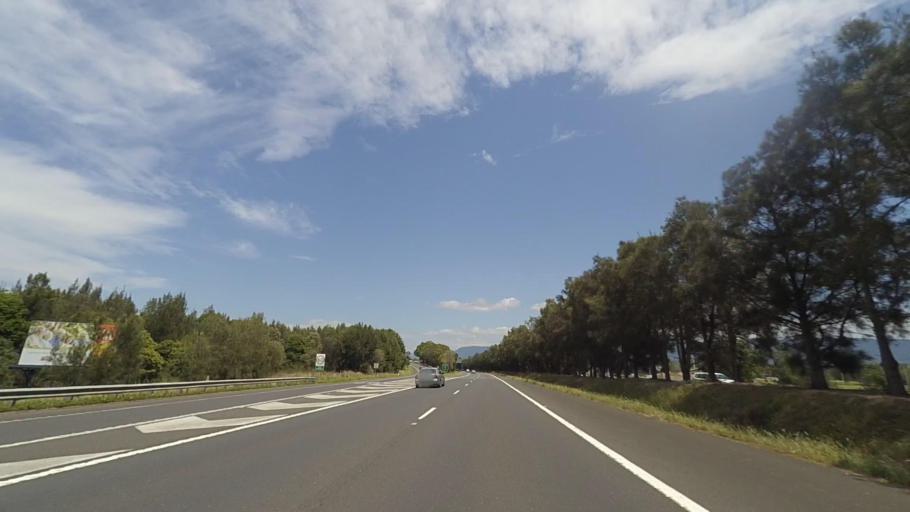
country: AU
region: New South Wales
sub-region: Wollongong
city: Koonawarra
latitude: -34.4861
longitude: 150.8125
